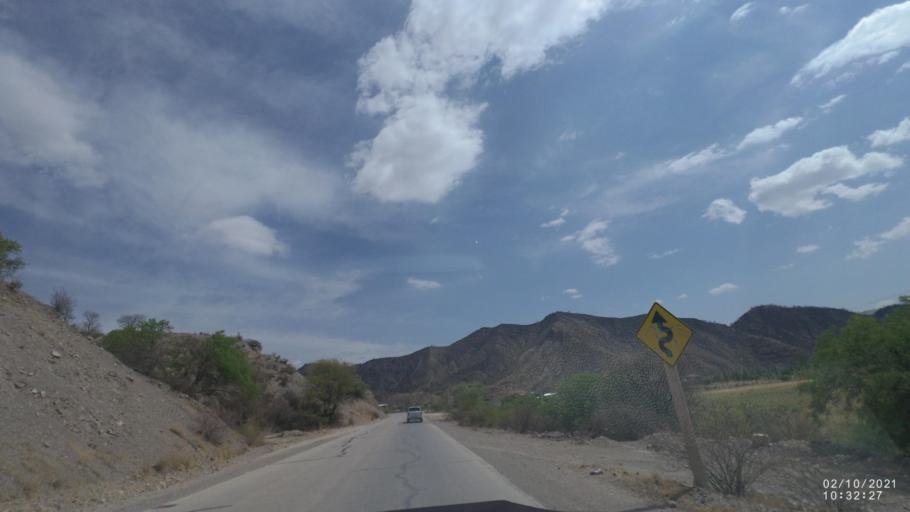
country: BO
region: Cochabamba
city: Capinota
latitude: -17.6882
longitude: -66.2582
